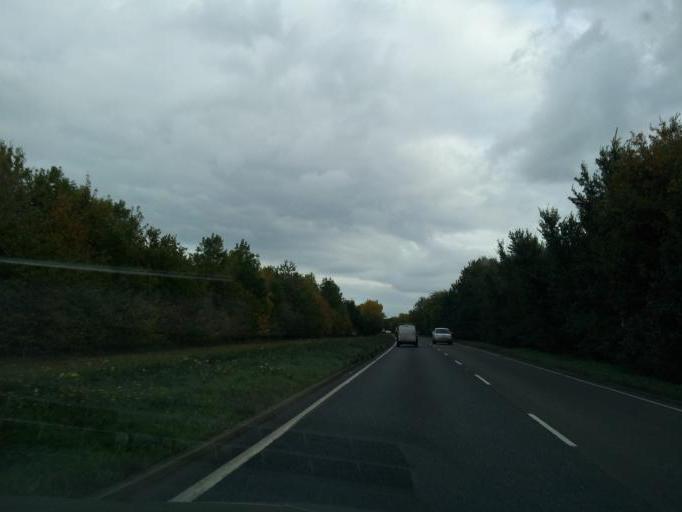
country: GB
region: England
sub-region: Cambridgeshire
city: Papworth Everard
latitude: 52.2280
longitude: -0.1155
